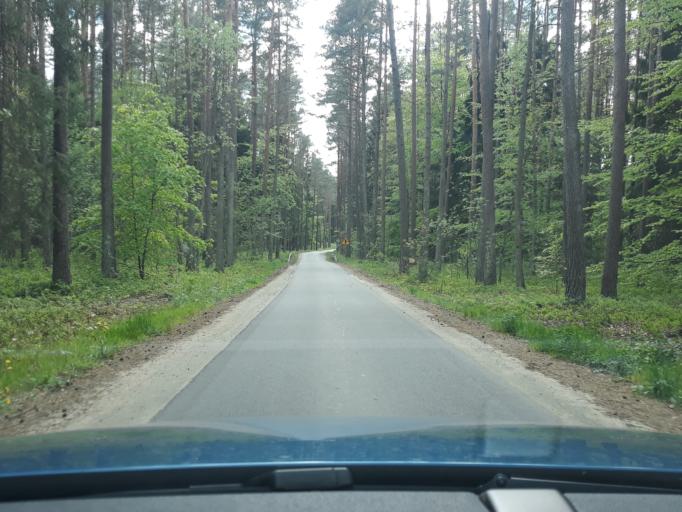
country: PL
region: Pomeranian Voivodeship
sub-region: Powiat czluchowski
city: Czluchow
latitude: 53.7439
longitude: 17.3546
